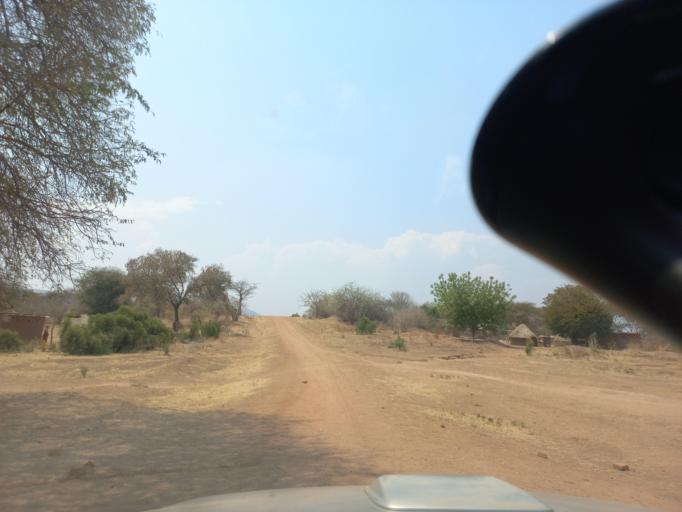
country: ZW
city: Chirundu
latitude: -15.9133
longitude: 28.6867
